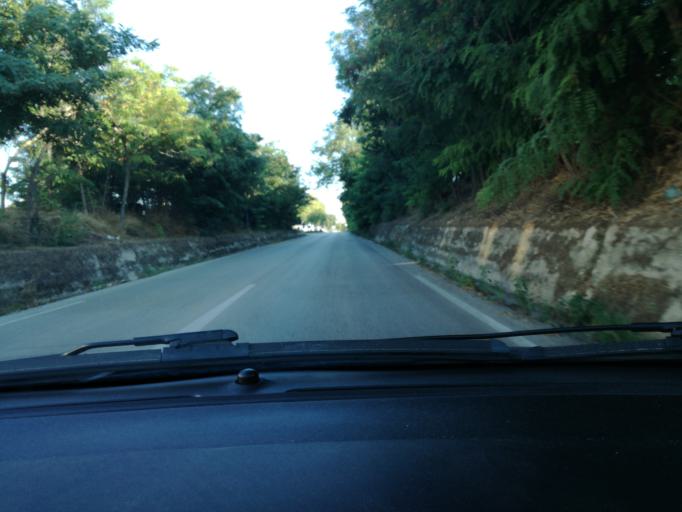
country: IT
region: Molise
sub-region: Provincia di Campobasso
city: San Giacomo degli Schiavoni
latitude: 41.9608
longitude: 14.9436
